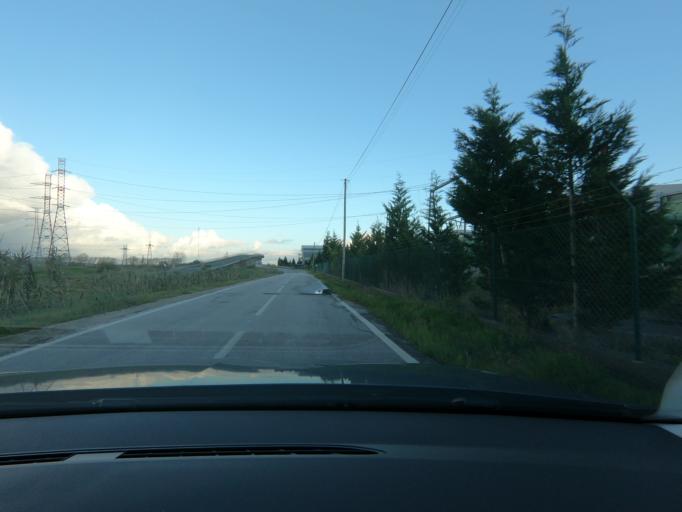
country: PT
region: Lisbon
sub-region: Alenquer
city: Carregado
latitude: 39.0132
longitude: -8.9522
